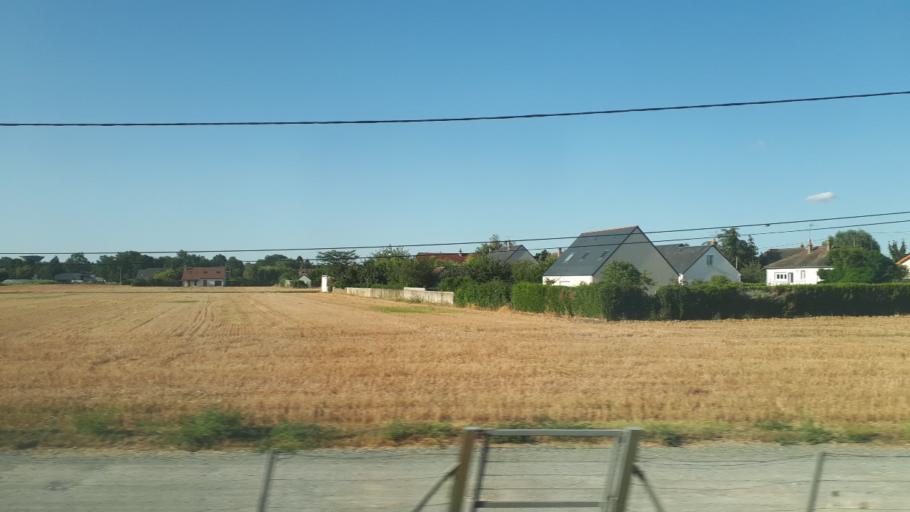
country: FR
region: Centre
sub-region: Departement d'Indre-et-Loire
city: La Ville-aux-Dames
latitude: 47.3908
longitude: 0.7786
